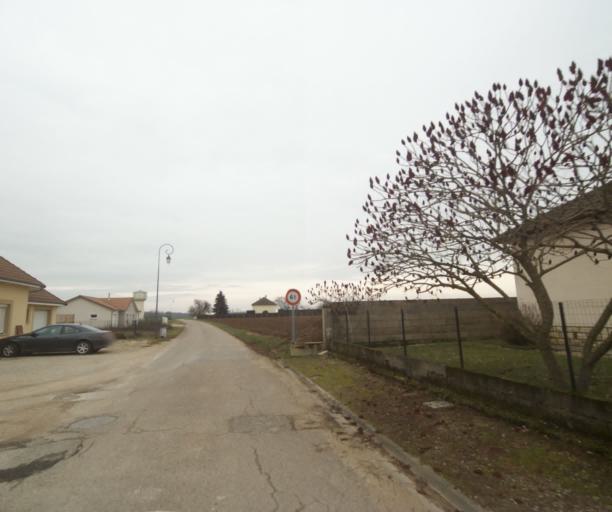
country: FR
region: Champagne-Ardenne
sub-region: Departement de la Haute-Marne
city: Villiers-en-Lieu
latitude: 48.6376
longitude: 4.7739
